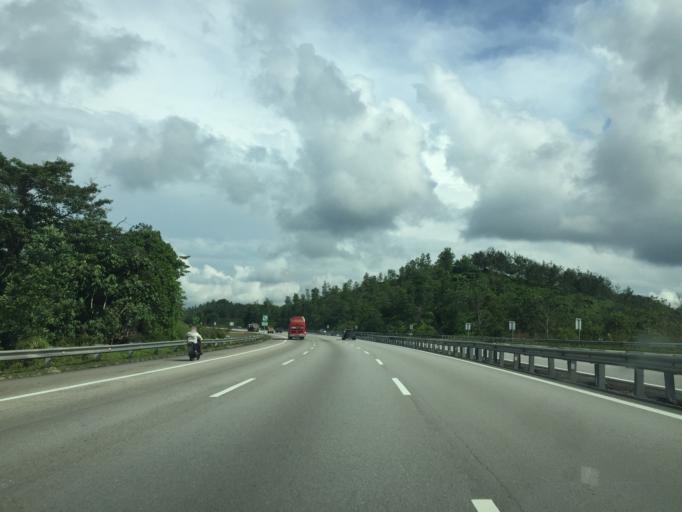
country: MY
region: Selangor
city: Serendah
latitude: 3.5123
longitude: 101.5280
